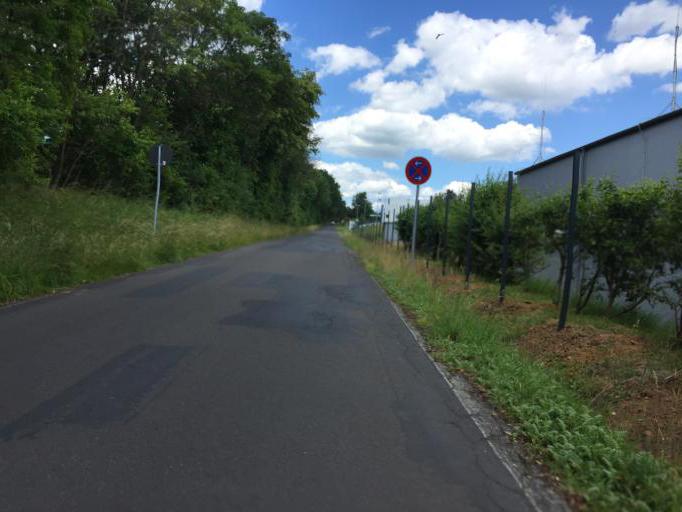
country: DE
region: Rheinland-Pfalz
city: Bannberscheid
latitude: 50.4521
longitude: 7.8299
